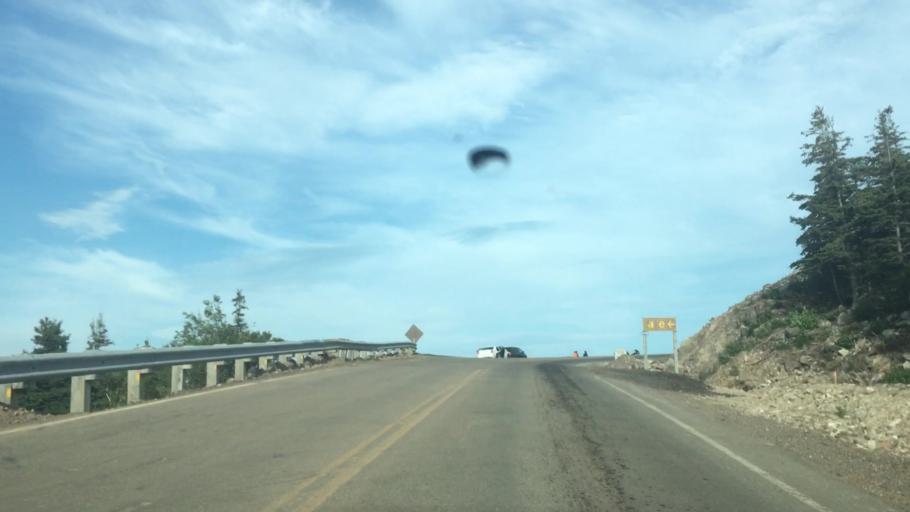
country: CA
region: Nova Scotia
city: Sydney Mines
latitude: 46.8197
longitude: -60.8331
